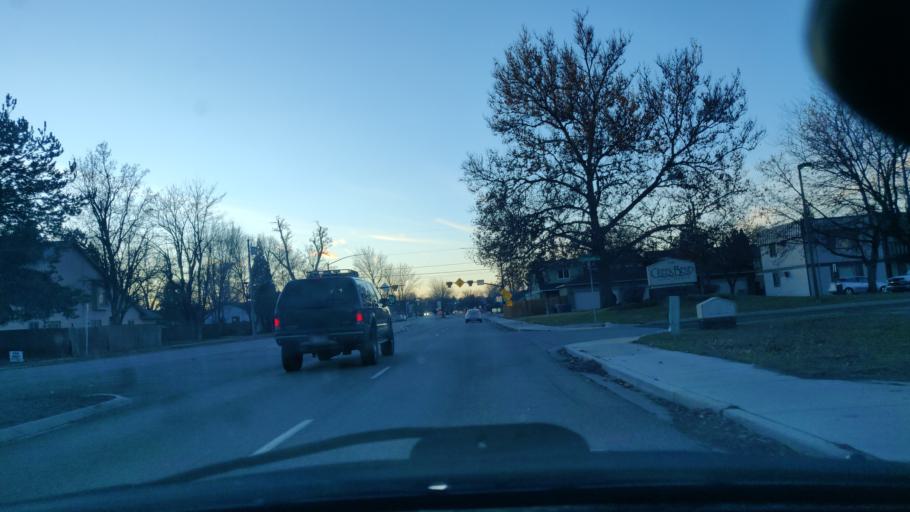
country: US
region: Idaho
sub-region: Ada County
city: Boise
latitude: 43.5986
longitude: -116.1895
